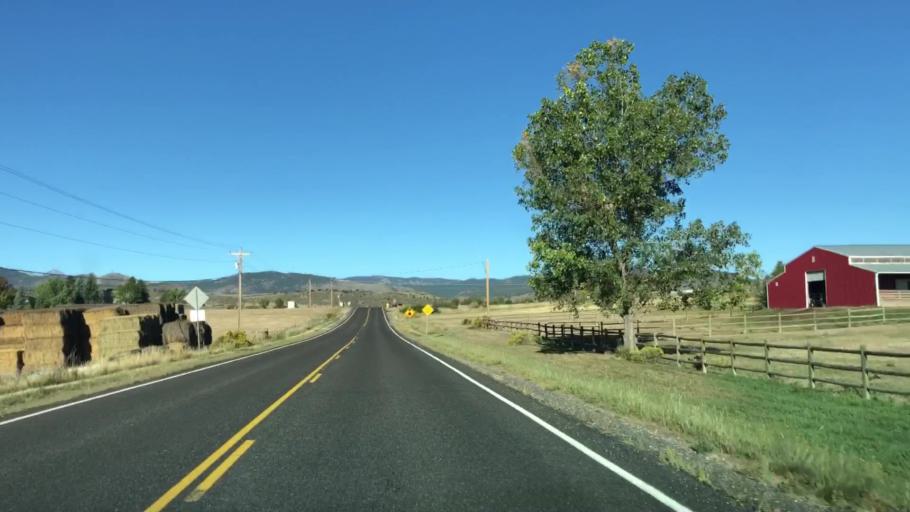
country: US
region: Colorado
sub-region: Larimer County
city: Loveland
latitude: 40.3785
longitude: -105.1601
